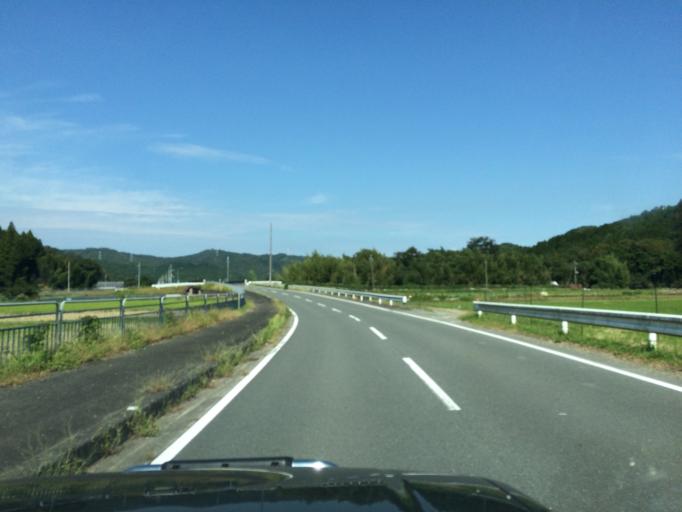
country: JP
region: Kyoto
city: Kameoka
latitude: 35.0909
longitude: 135.4446
